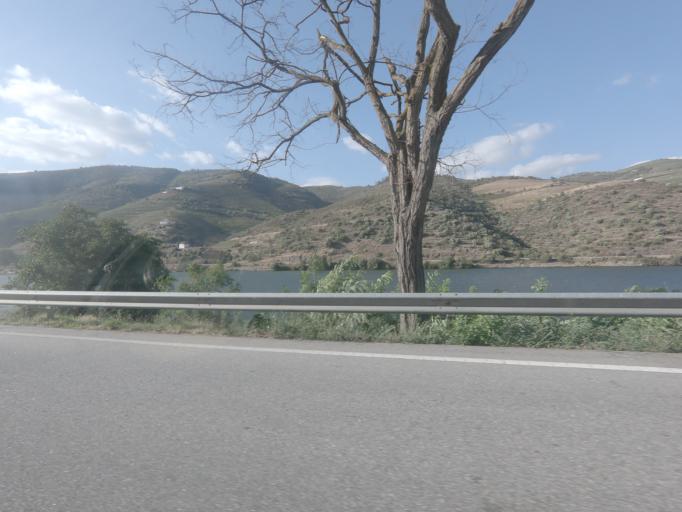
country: PT
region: Viseu
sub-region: Tabuaco
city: Tabuaco
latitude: 41.1577
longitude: -7.6070
